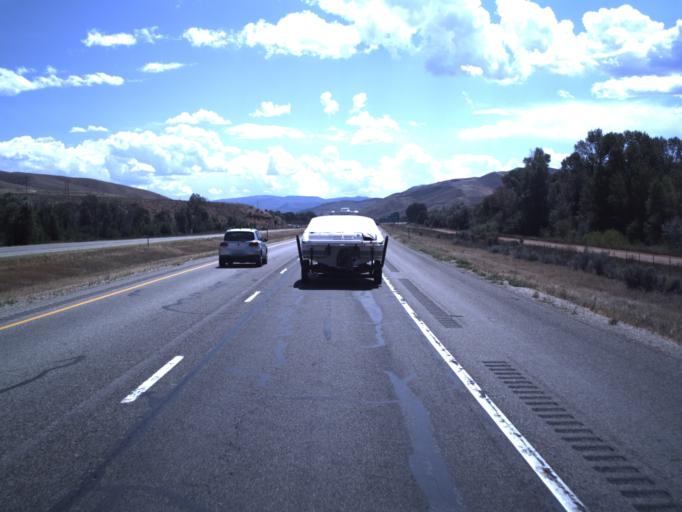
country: US
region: Utah
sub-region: Summit County
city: Coalville
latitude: 41.0273
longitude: -111.4994
